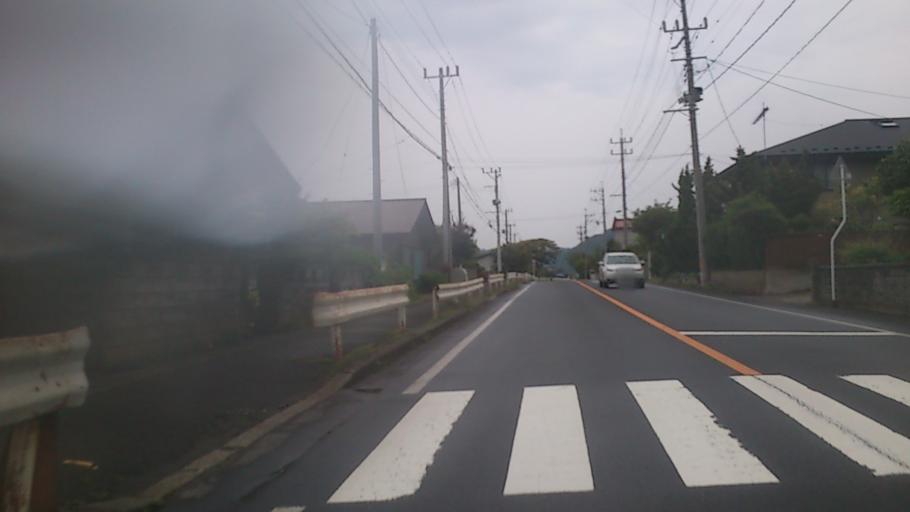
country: JP
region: Akita
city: Noshiromachi
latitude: 40.5411
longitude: 139.9464
